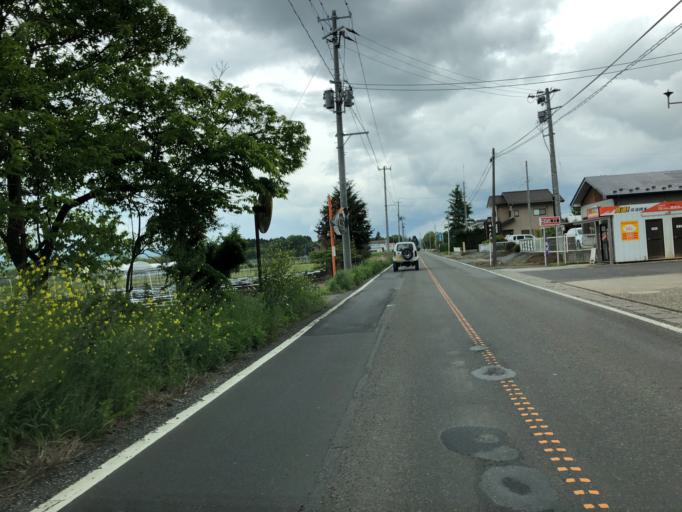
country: JP
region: Fukushima
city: Ishikawa
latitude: 37.1951
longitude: 140.3773
